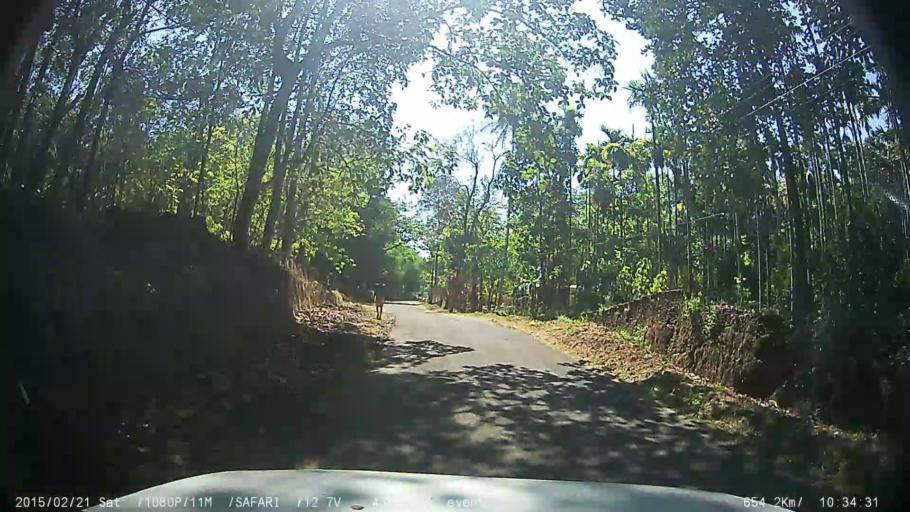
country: IN
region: Kerala
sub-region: Kottayam
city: Lalam
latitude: 9.8276
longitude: 76.7187
